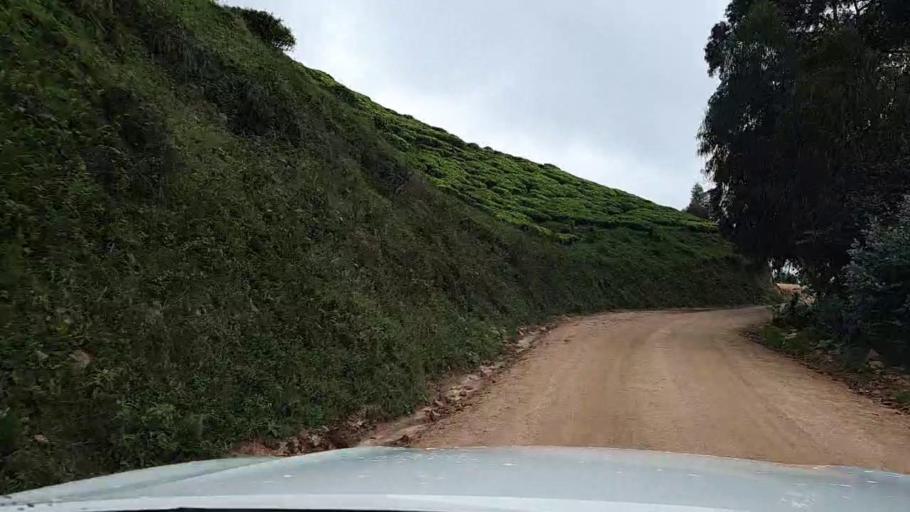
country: RW
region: Western Province
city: Kibuye
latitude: -2.2973
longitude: 29.3830
